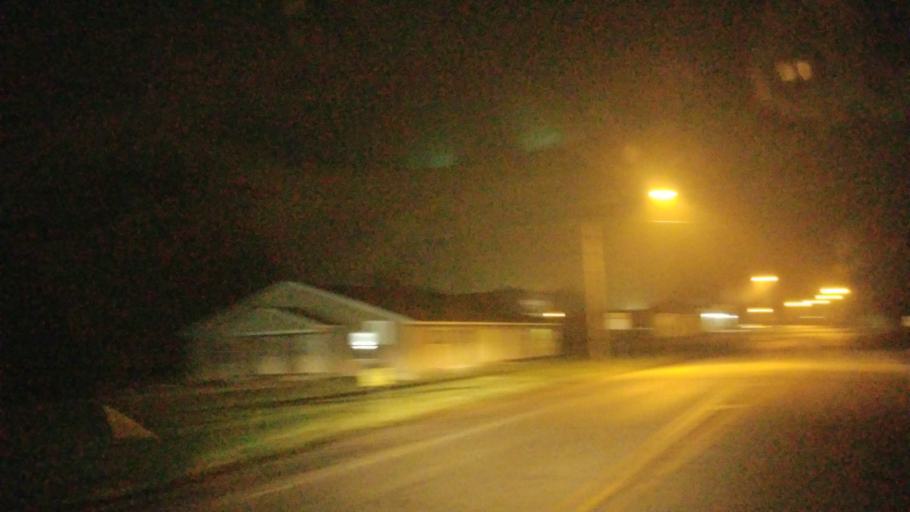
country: US
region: Missouri
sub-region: Pike County
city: Bowling Green
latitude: 39.3412
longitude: -91.2028
